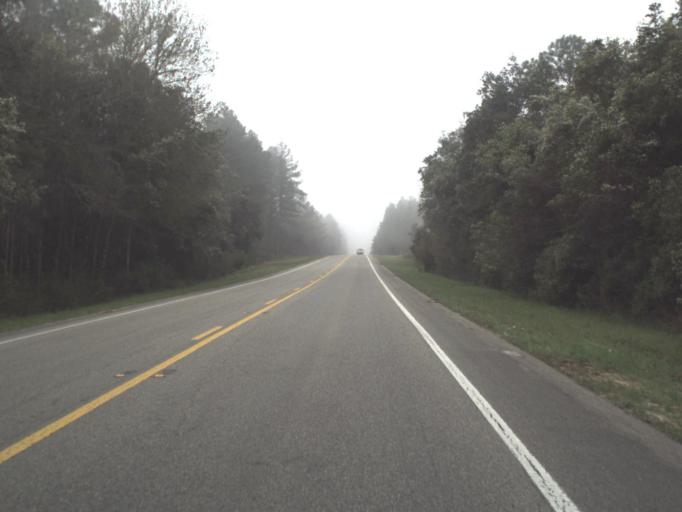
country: US
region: Florida
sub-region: Gadsden County
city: Gretna
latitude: 30.4938
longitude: -84.7195
